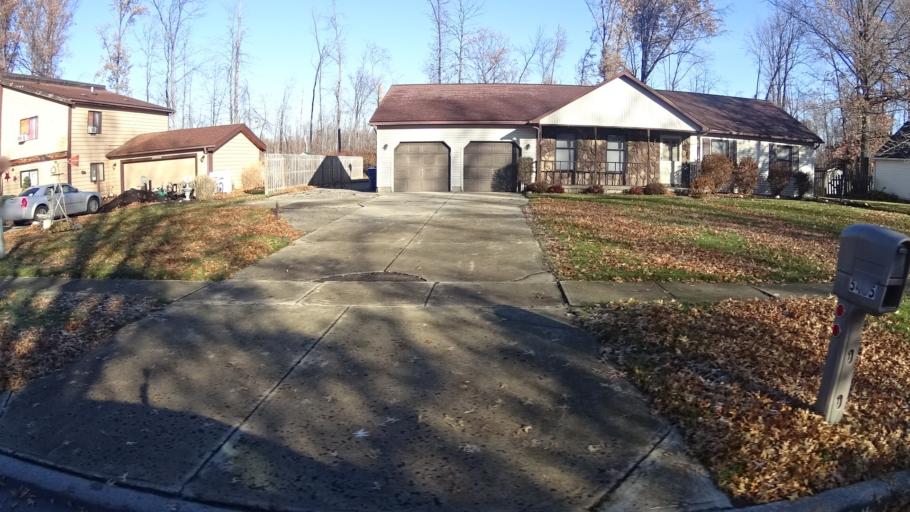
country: US
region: Ohio
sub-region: Lorain County
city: Avon
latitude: 41.4603
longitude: -82.0711
